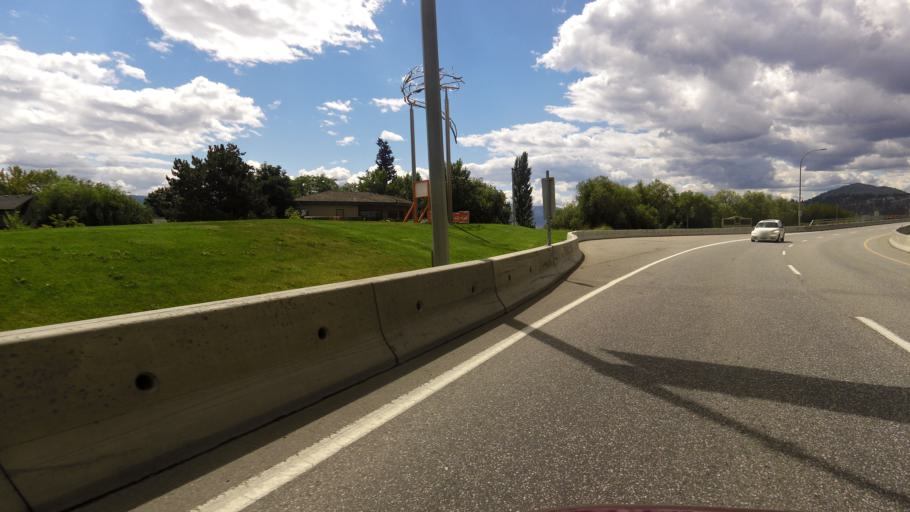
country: CA
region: British Columbia
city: Kelowna
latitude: 49.8813
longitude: -119.5019
